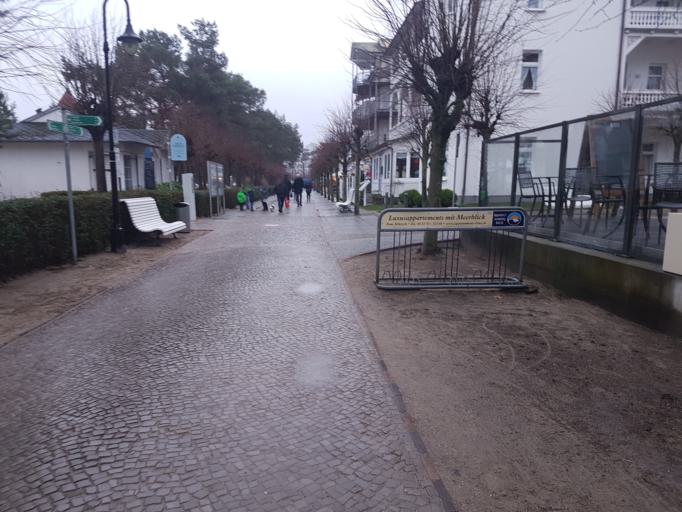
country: DE
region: Mecklenburg-Vorpommern
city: Ostseebad Binz
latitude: 54.4064
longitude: 13.6071
